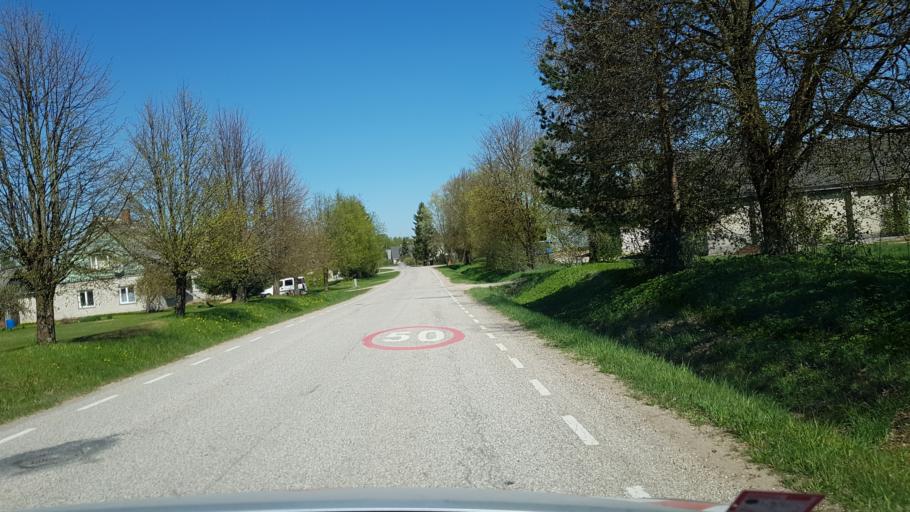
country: EE
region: Vorumaa
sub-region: Antsla vald
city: Vana-Antsla
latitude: 57.8190
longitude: 26.5207
